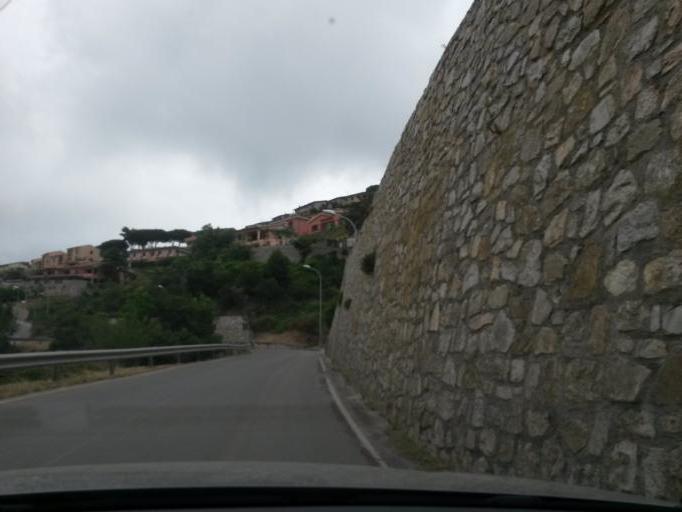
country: IT
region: Tuscany
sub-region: Provincia di Livorno
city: Capoliveri
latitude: 42.7404
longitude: 10.3780
